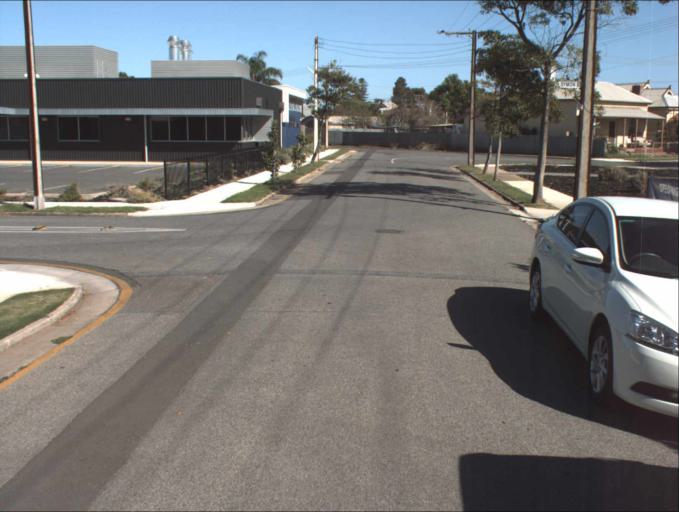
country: AU
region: South Australia
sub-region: Port Adelaide Enfield
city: Alberton
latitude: -34.8569
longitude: 138.5213
